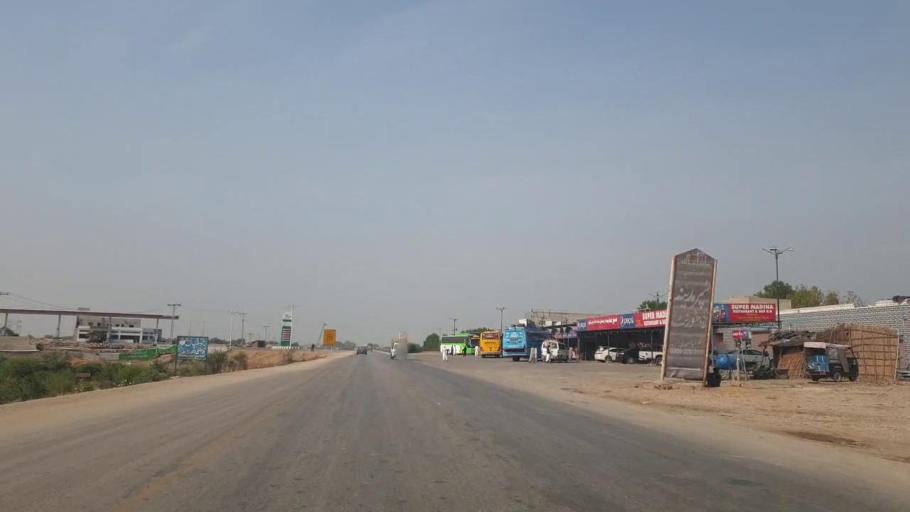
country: PK
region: Sindh
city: Sann
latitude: 26.1593
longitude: 68.0217
